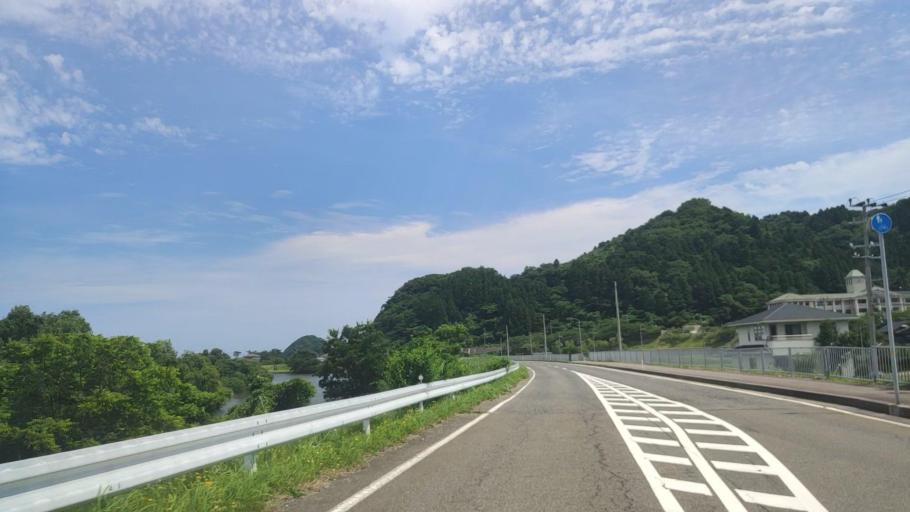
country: JP
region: Hyogo
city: Toyooka
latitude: 35.6489
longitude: 134.7637
